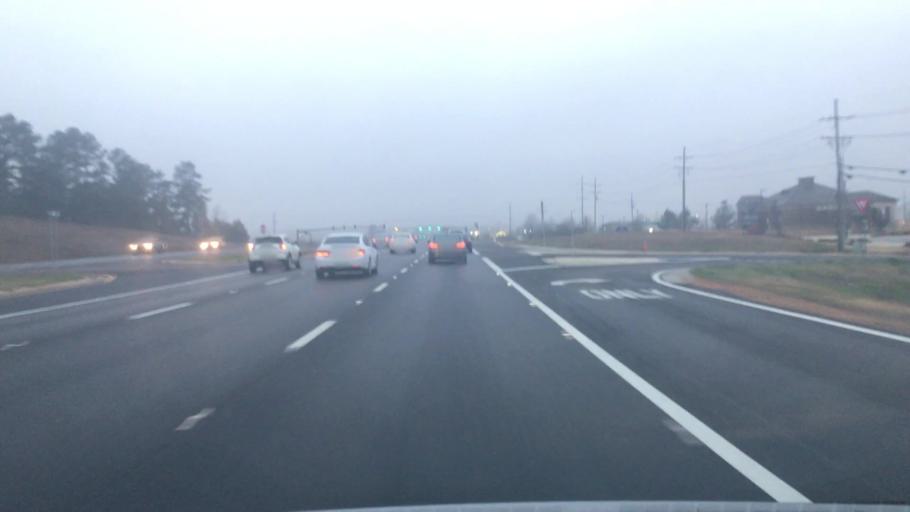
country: US
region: Mississippi
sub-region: Rankin County
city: Flowood
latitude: 32.3431
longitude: -90.0558
